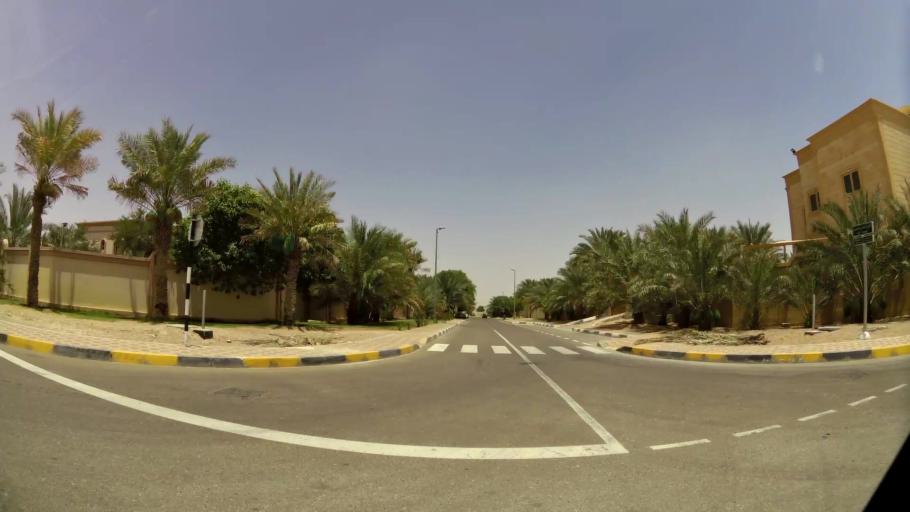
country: OM
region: Al Buraimi
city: Al Buraymi
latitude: 24.2684
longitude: 55.7166
